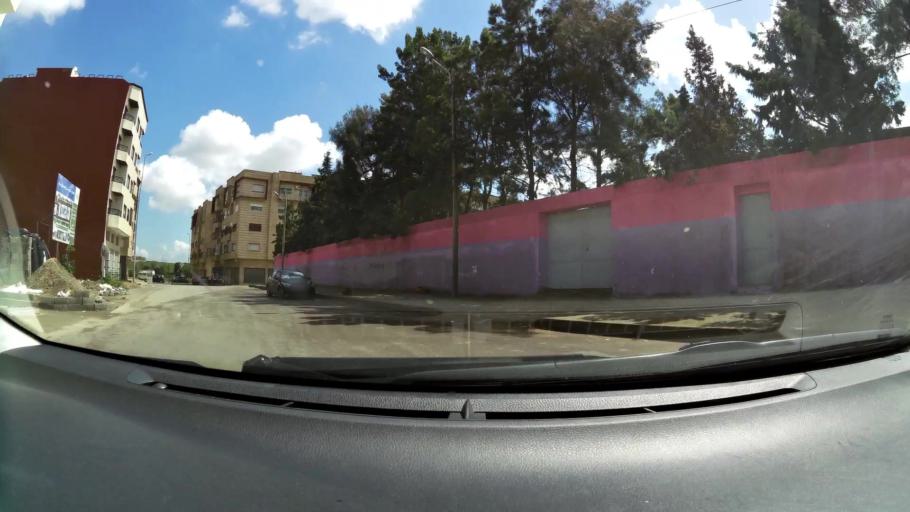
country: MA
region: Grand Casablanca
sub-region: Casablanca
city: Casablanca
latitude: 33.5398
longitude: -7.5608
